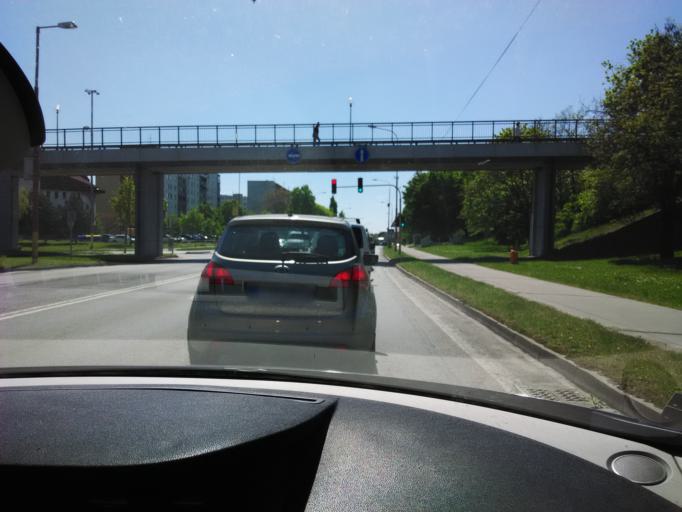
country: SK
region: Trnavsky
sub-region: Okres Trnava
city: Trnava
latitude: 48.3797
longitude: 17.5929
